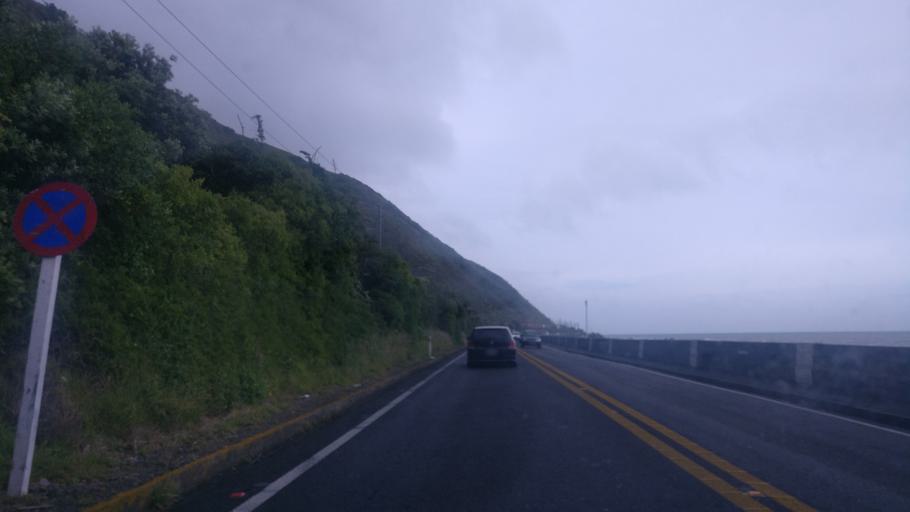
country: NZ
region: Wellington
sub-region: Kapiti Coast District
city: Paraparaumu
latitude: -41.0021
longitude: 174.9359
